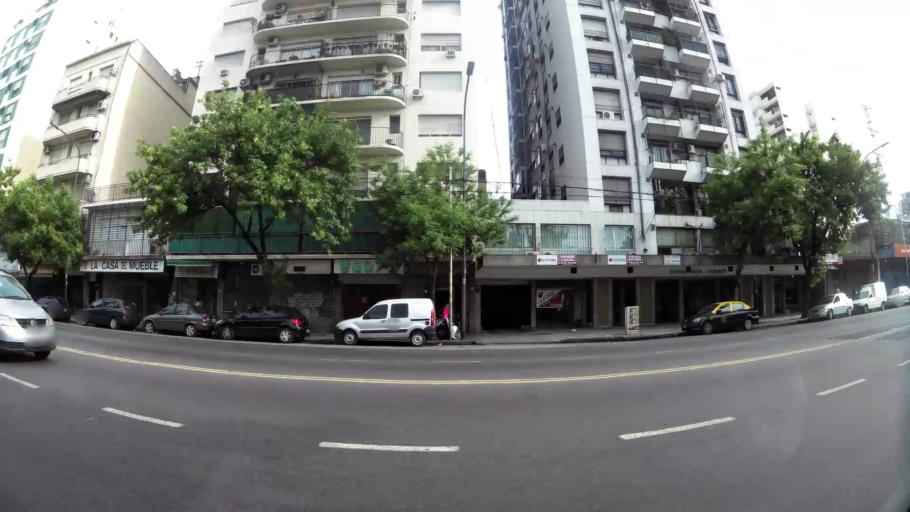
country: AR
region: Buenos Aires F.D.
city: Villa Santa Rita
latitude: -34.6336
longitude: -58.4812
